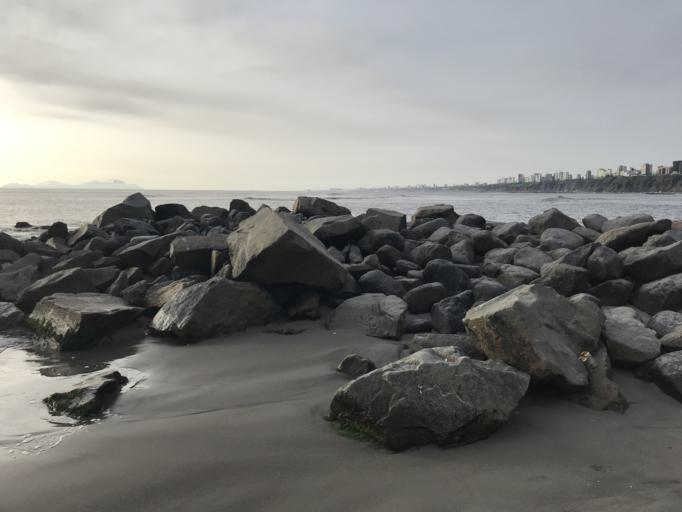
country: PE
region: Lima
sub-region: Lima
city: Surco
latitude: -12.1520
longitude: -77.0254
